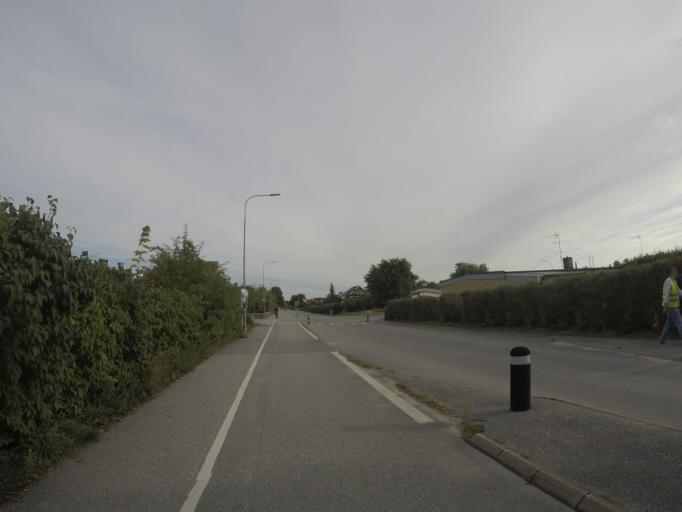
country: SE
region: OErebro
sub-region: Orebro Kommun
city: Orebro
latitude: 59.2589
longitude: 15.2485
